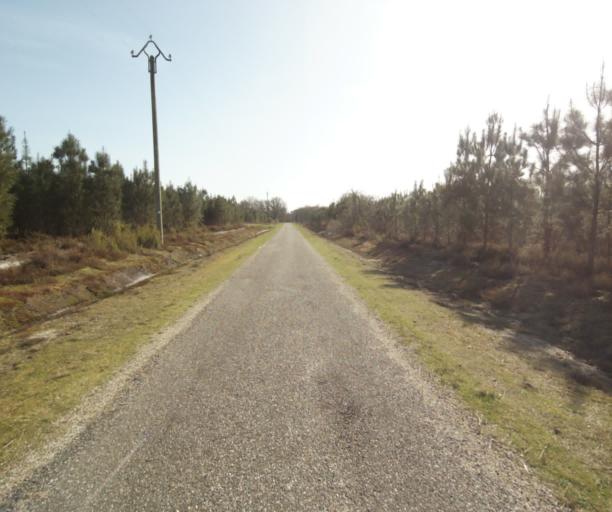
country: FR
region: Aquitaine
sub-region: Departement des Landes
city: Roquefort
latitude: 44.1316
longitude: -0.1934
